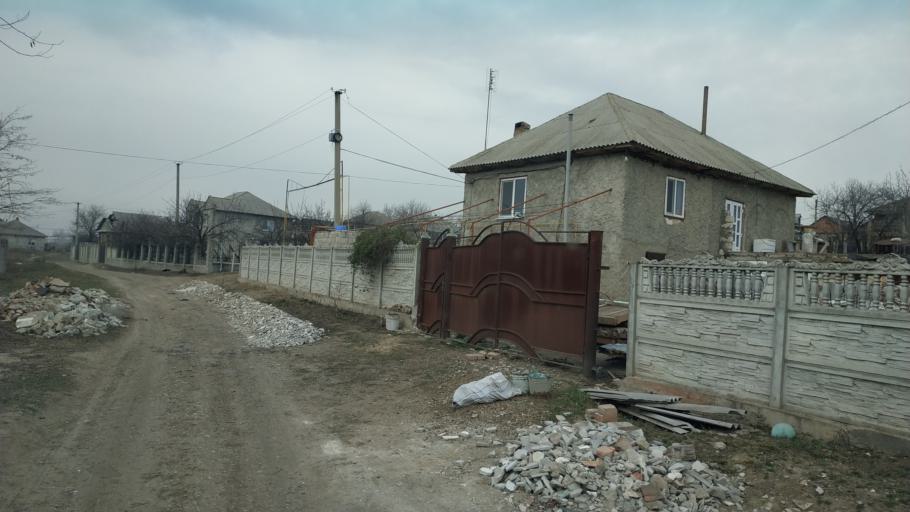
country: MD
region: Chisinau
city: Singera
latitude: 46.9374
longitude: 28.9903
